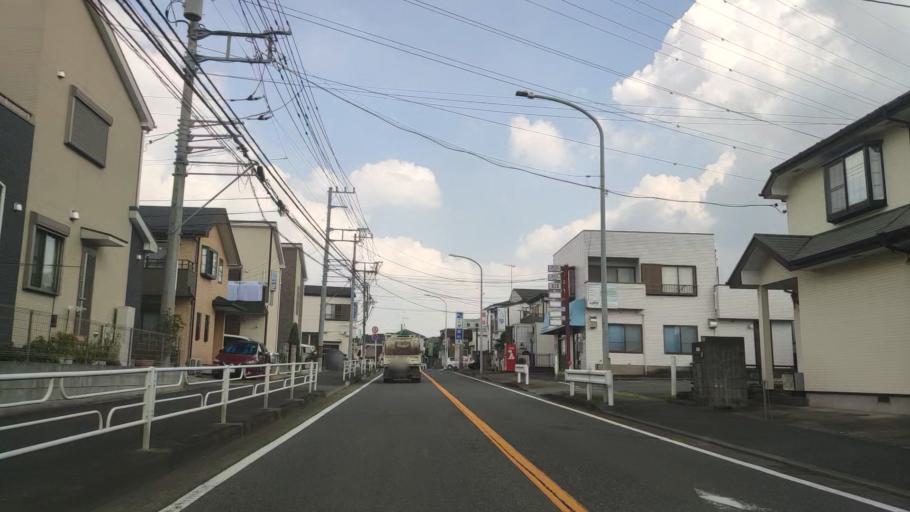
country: JP
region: Kanagawa
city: Minami-rinkan
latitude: 35.4519
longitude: 139.5027
